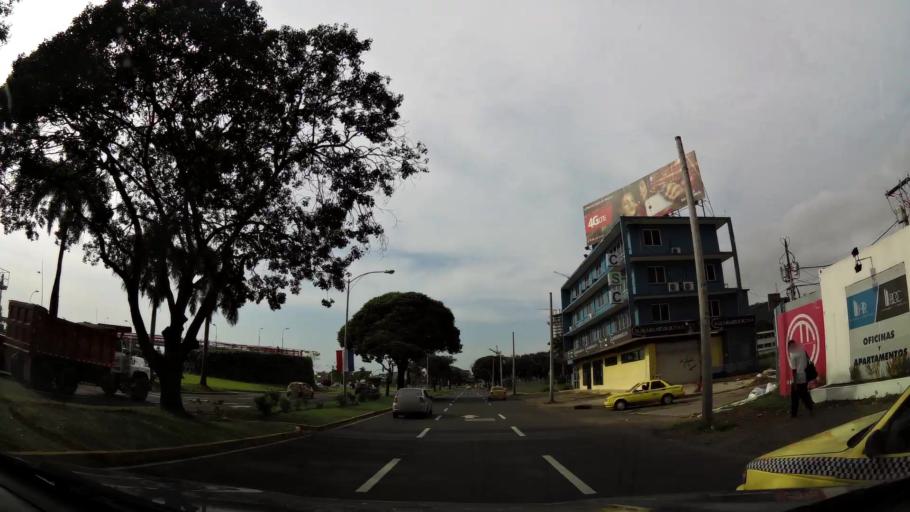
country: PA
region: Panama
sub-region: Distrito de Panama
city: Ancon
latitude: 8.9633
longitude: -79.5356
